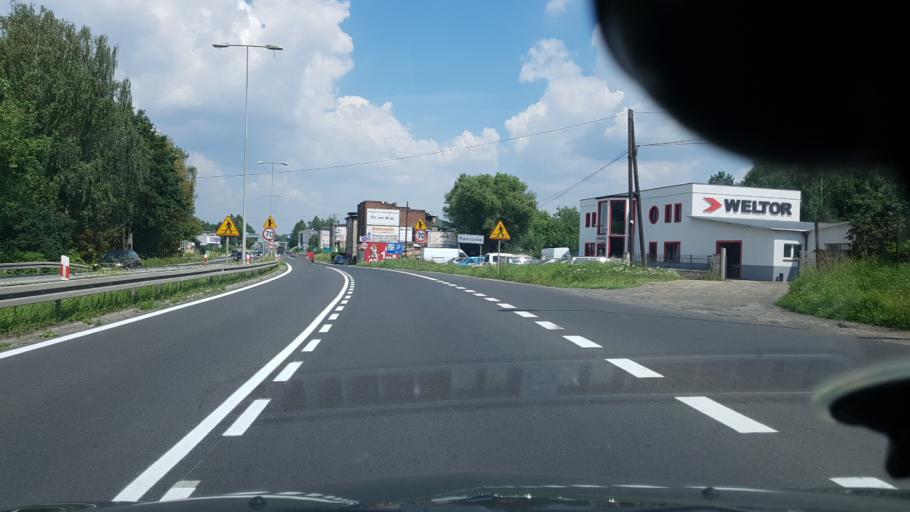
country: PL
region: Silesian Voivodeship
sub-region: Powiat mikolowski
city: Mikolow
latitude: 50.1796
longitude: 18.9095
